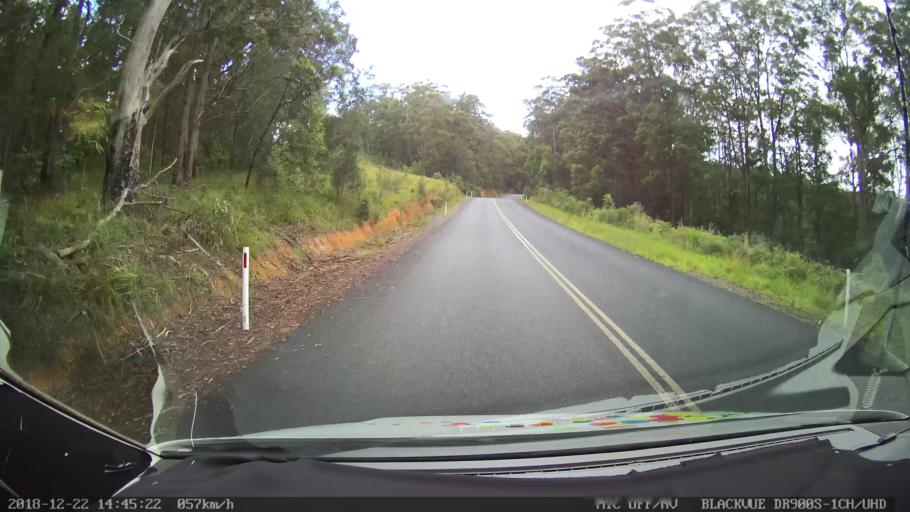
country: AU
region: New South Wales
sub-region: Bellingen
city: Dorrigo
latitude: -30.1699
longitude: 152.5697
